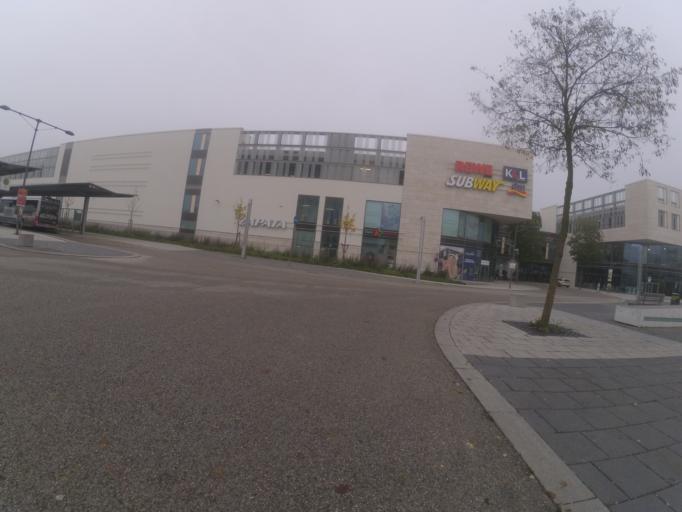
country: DE
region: Bavaria
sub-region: Swabia
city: Neu-Ulm
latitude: 48.3925
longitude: 10.0037
